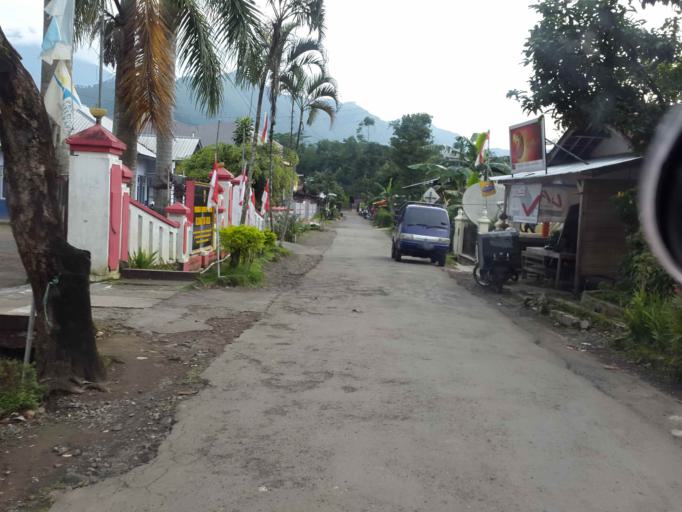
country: ID
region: Central Java
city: Randudongkal
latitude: -7.1858
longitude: 109.3292
